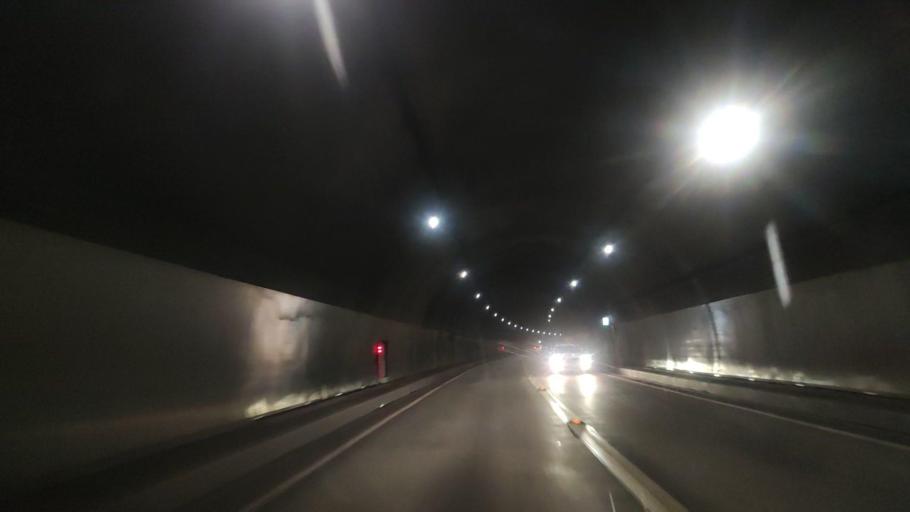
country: JP
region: Nagano
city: Okaya
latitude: 36.0948
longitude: 138.0829
